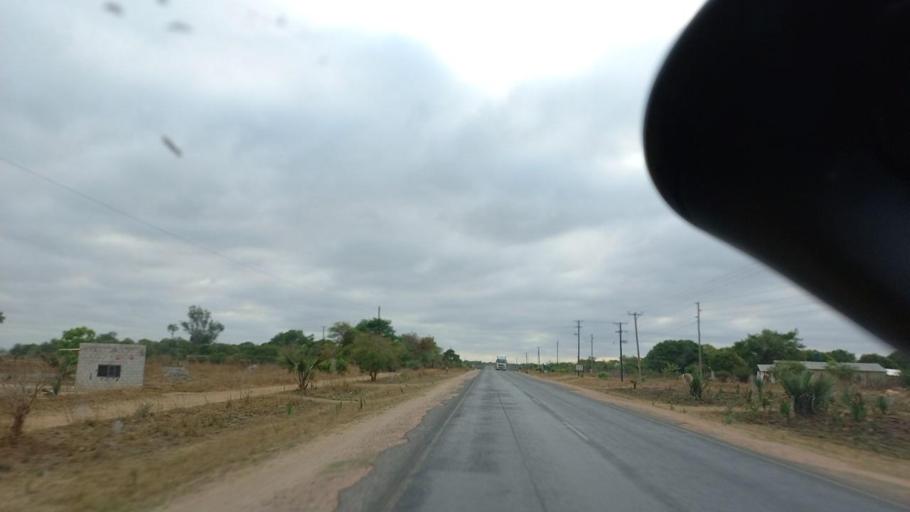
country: ZM
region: Lusaka
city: Chongwe
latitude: -15.3406
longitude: 28.6226
